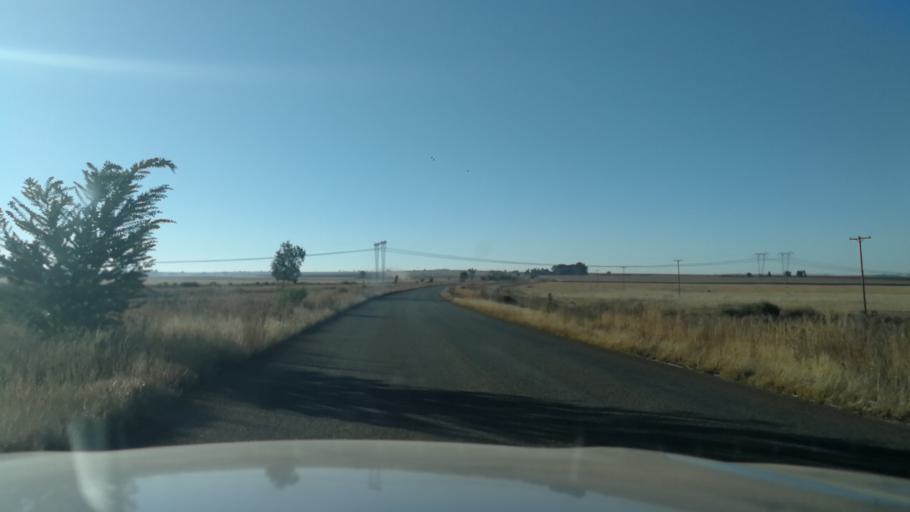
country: ZA
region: North-West
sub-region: Bojanala Platinum District Municipality
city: Rustenburg
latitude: -25.9727
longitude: 27.2427
